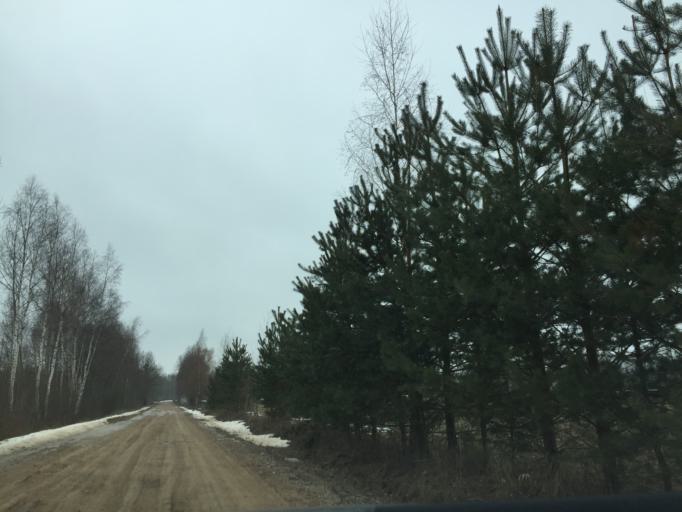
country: LV
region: Lecava
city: Iecava
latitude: 56.5681
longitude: 24.0545
